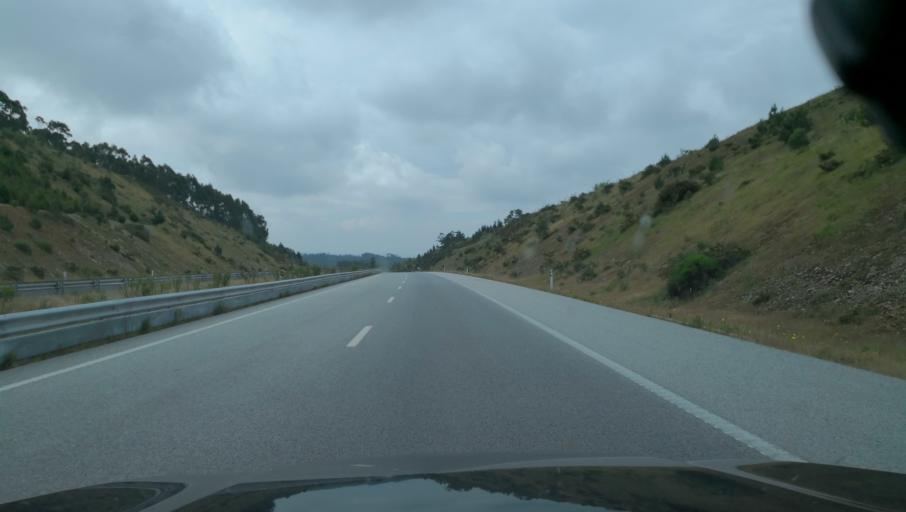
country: PT
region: Coimbra
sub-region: Figueira da Foz
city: Alhadas
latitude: 40.1868
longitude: -8.8107
